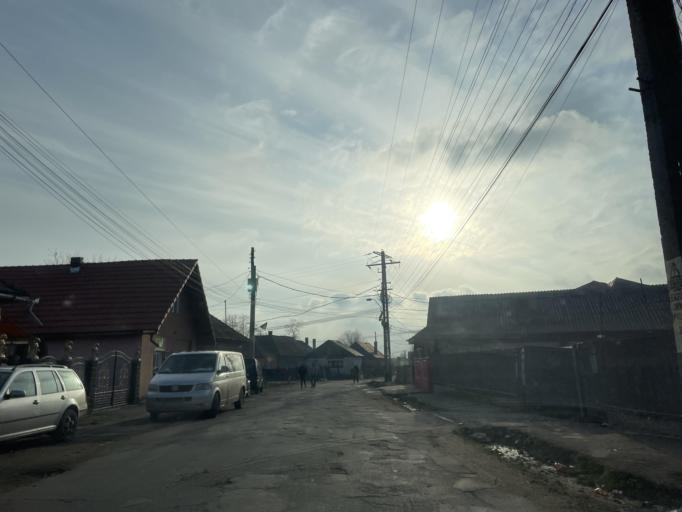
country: RO
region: Mures
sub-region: Municipiul Reghin
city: Apalina
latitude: 46.7599
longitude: 24.6904
